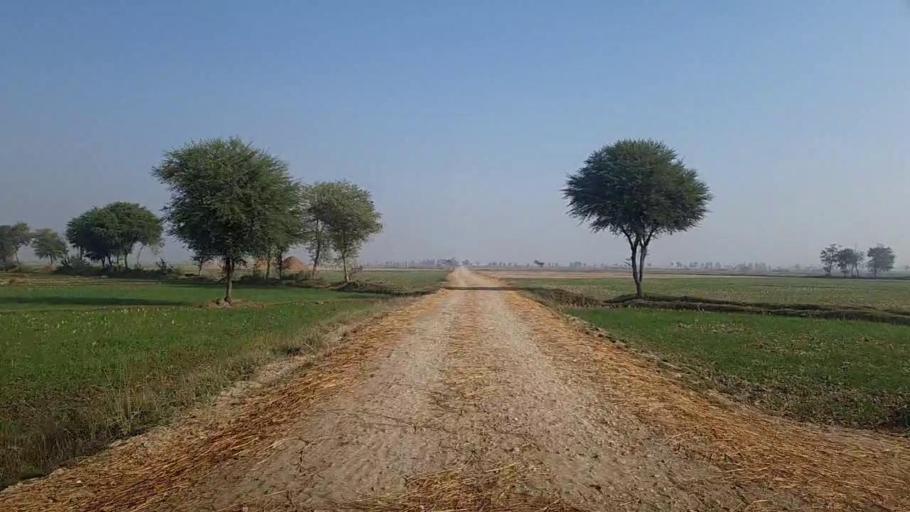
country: PK
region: Sindh
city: Radhan
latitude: 27.1206
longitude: 67.8973
